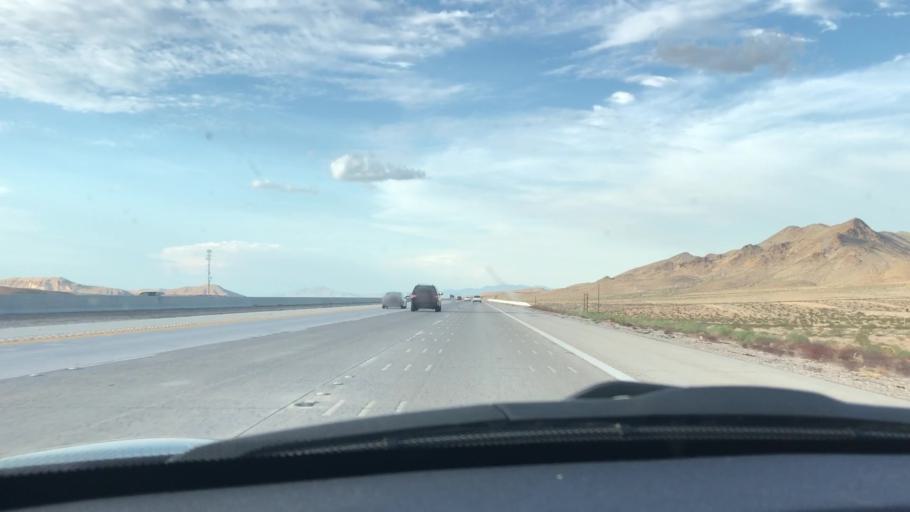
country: US
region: Nevada
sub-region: Clark County
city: Enterprise
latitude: 35.8778
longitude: -115.2348
